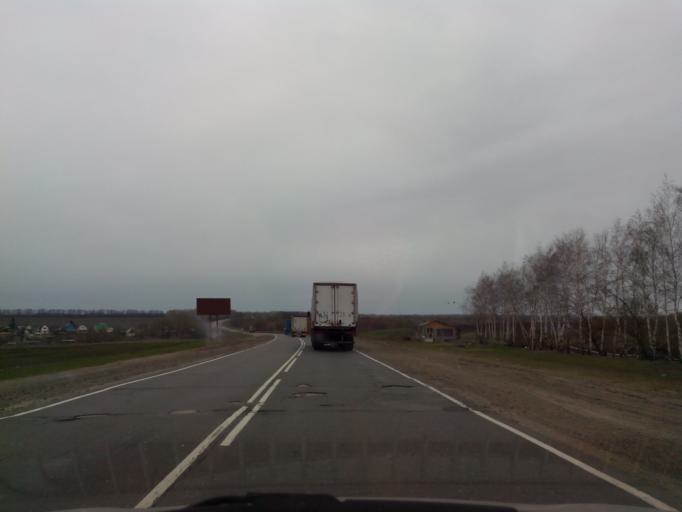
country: RU
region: Tambov
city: Pokrovo-Prigorodnoye
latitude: 52.6741
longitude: 41.3319
